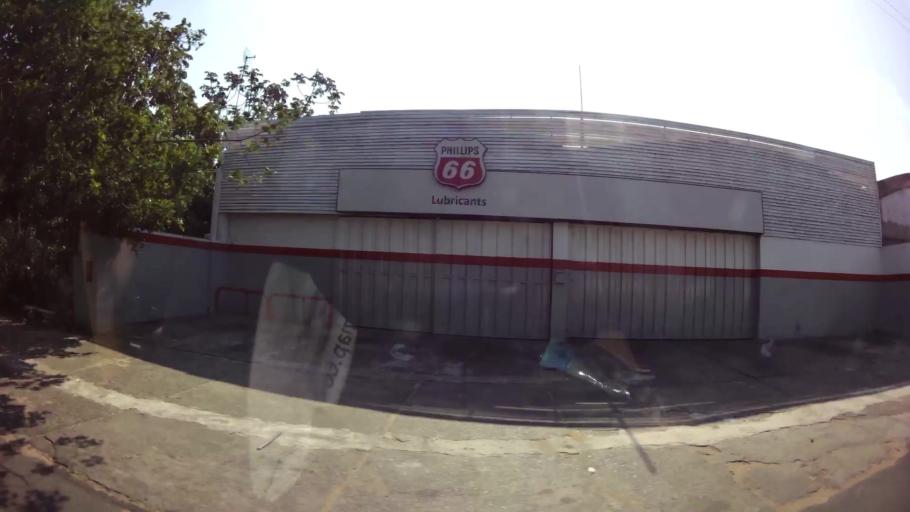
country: PY
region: Asuncion
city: Asuncion
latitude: -25.3016
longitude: -57.6326
